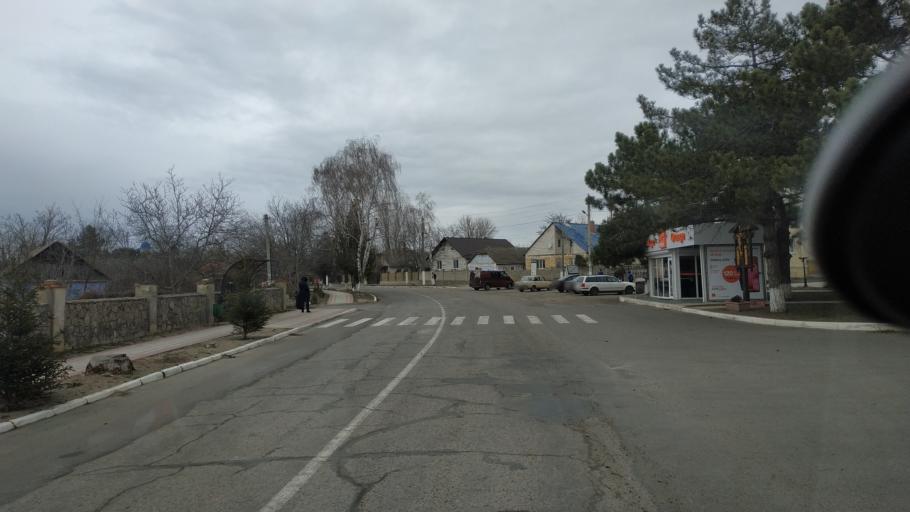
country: MD
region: Telenesti
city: Cocieri
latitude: 47.3060
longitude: 29.1119
